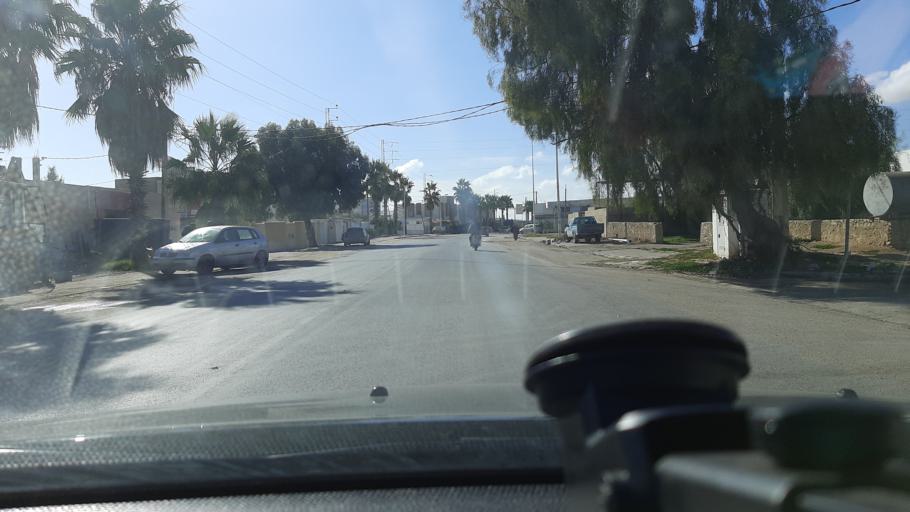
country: TN
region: Safaqis
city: Sfax
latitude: 34.8095
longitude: 10.7068
